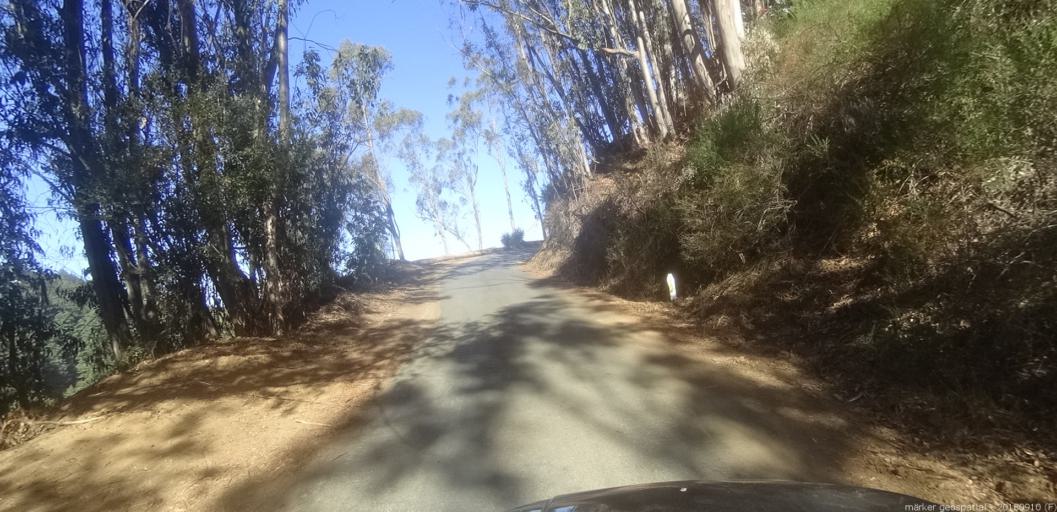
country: US
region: California
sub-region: Monterey County
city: Carmel Valley Village
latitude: 36.3986
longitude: -121.8822
